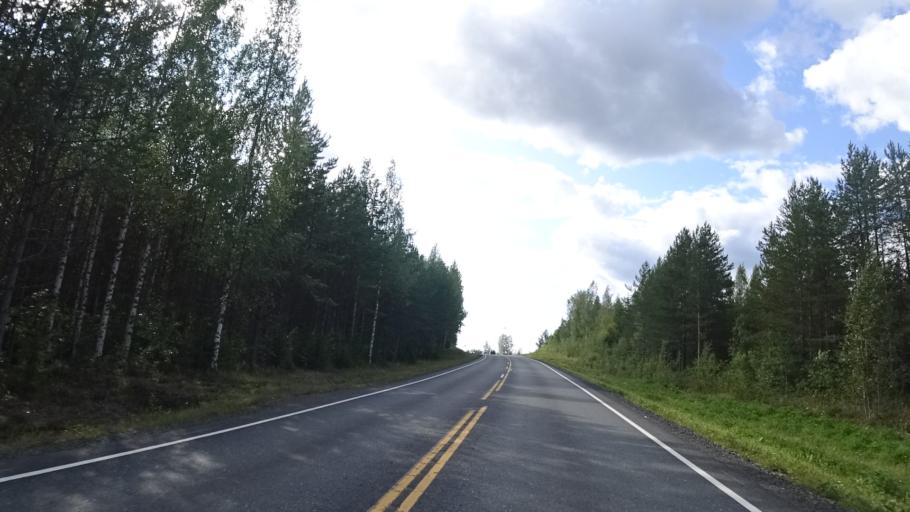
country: FI
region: North Karelia
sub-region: Keski-Karjala
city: Tohmajaervi
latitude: 62.1852
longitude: 30.4983
